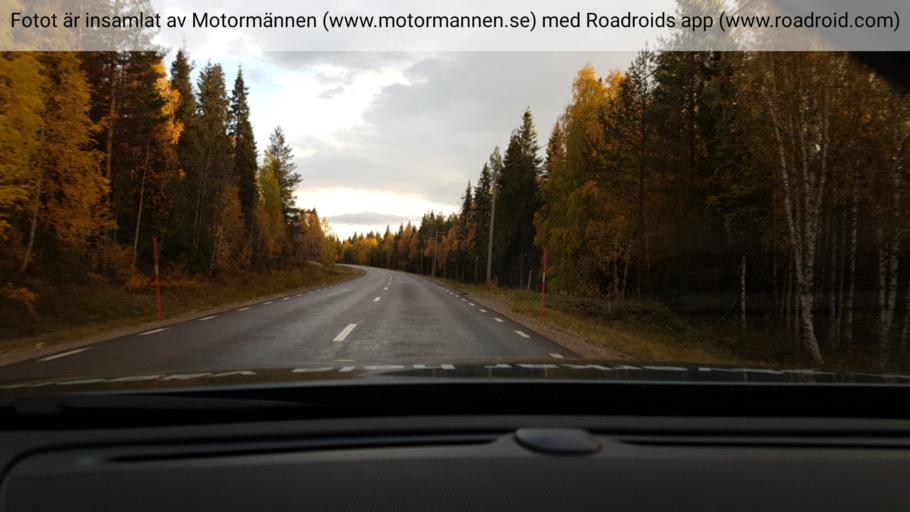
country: SE
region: Norrbotten
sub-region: Overkalix Kommun
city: OEverkalix
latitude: 66.5920
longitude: 22.7564
